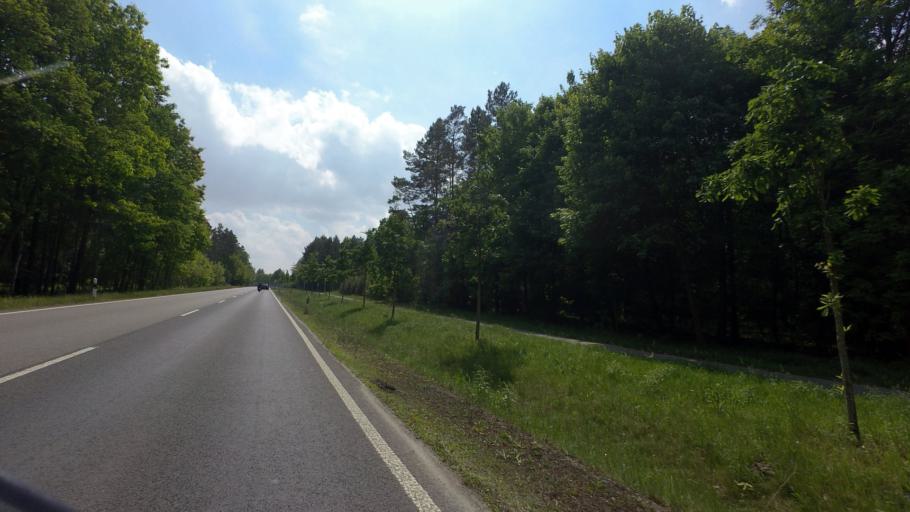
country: DE
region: Saxony
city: Weisskeissel
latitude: 51.4789
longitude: 14.7226
